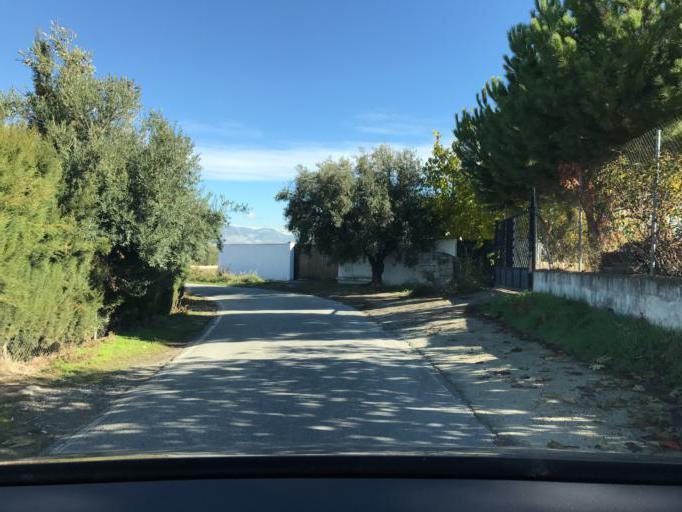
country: ES
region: Andalusia
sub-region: Provincia de Granada
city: Cullar-Vega
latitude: 37.1454
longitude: -3.6612
